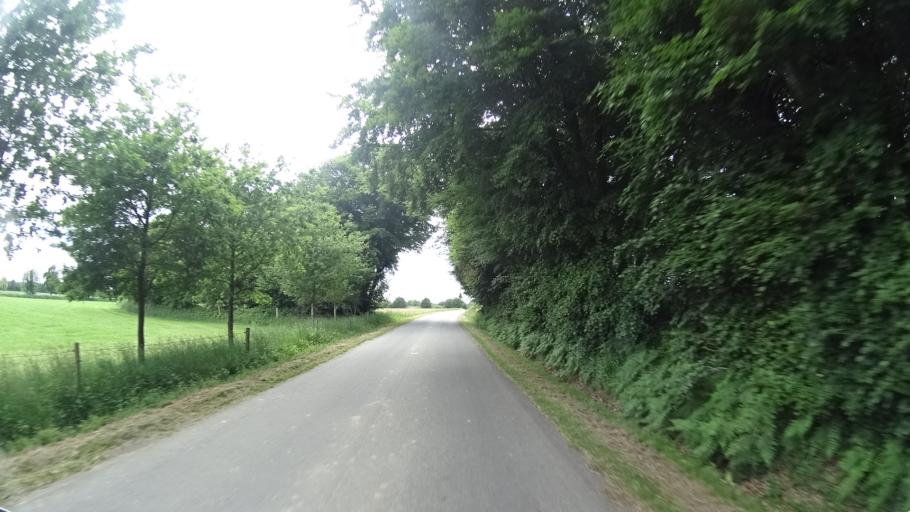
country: FR
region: Brittany
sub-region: Departement d'Ille-et-Vilaine
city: Plelan-le-Grand
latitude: 48.0465
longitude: -2.0818
